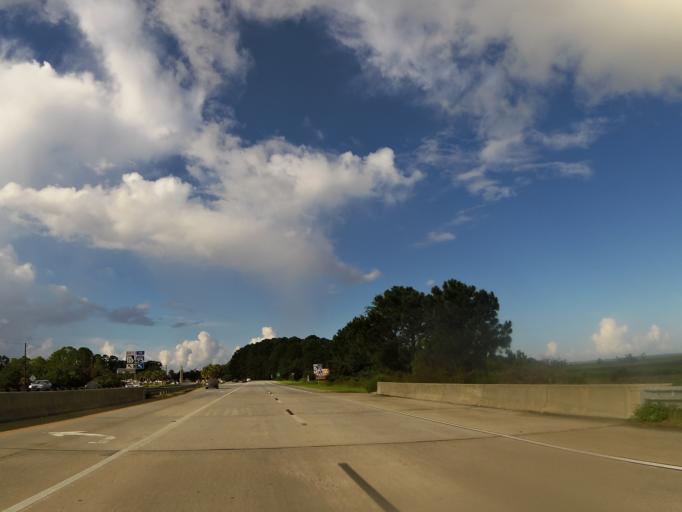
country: US
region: Georgia
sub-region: Glynn County
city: Country Club Estates
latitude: 31.1828
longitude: -81.4708
